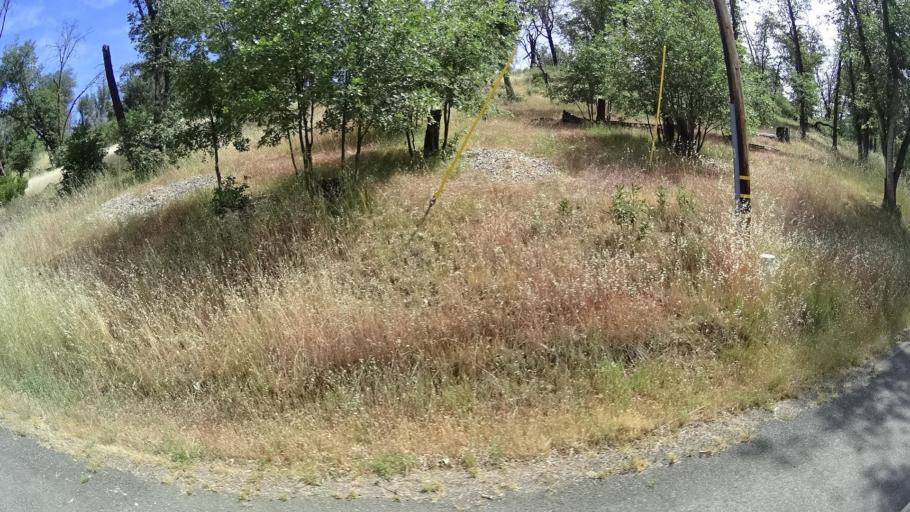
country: US
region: California
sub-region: Lake County
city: Cobb
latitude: 38.8746
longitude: -122.6753
